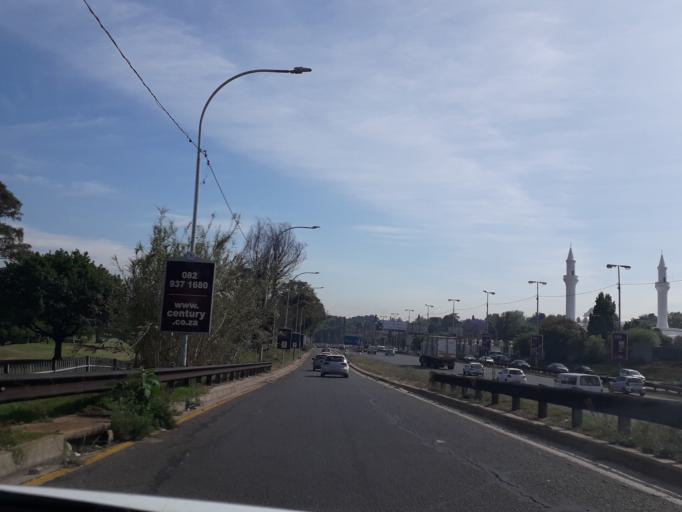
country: ZA
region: Gauteng
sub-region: City of Johannesburg Metropolitan Municipality
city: Johannesburg
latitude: -26.1648
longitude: 28.0557
